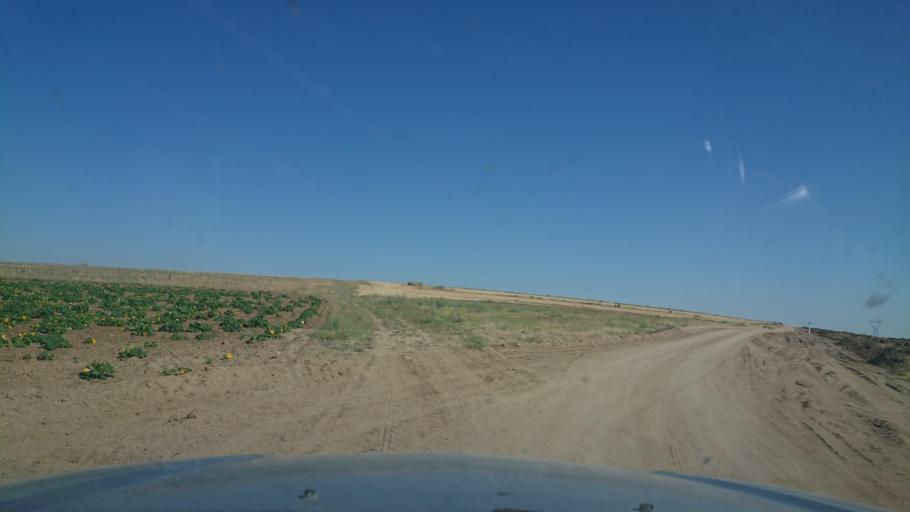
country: TR
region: Aksaray
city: Agacoren
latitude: 38.8372
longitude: 33.9444
